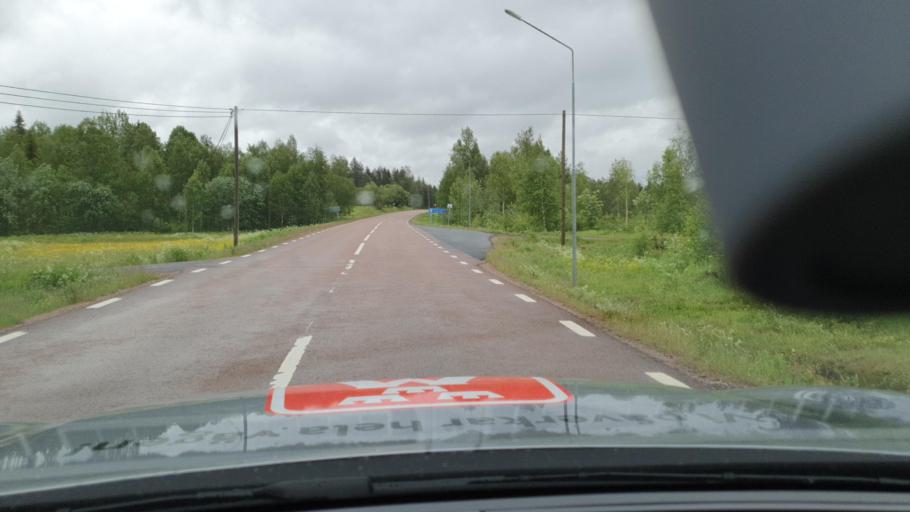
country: FI
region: Lapland
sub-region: Torniolaakso
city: Ylitornio
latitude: 66.1631
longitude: 23.8551
